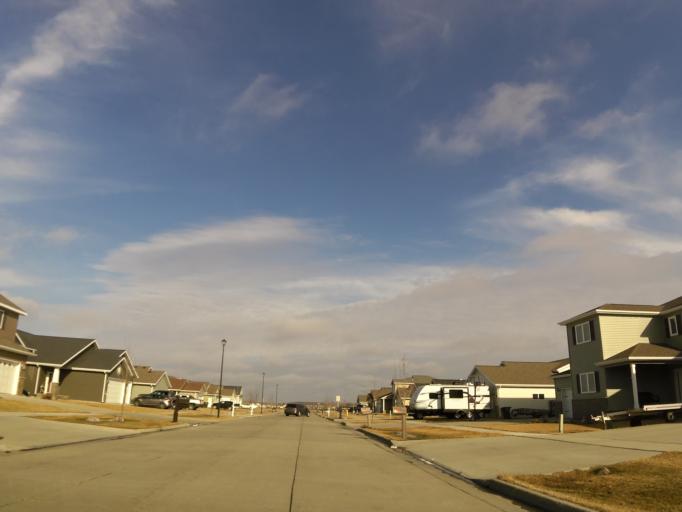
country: US
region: North Dakota
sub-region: Grand Forks County
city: Grand Forks
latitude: 47.8805
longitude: -97.0601
